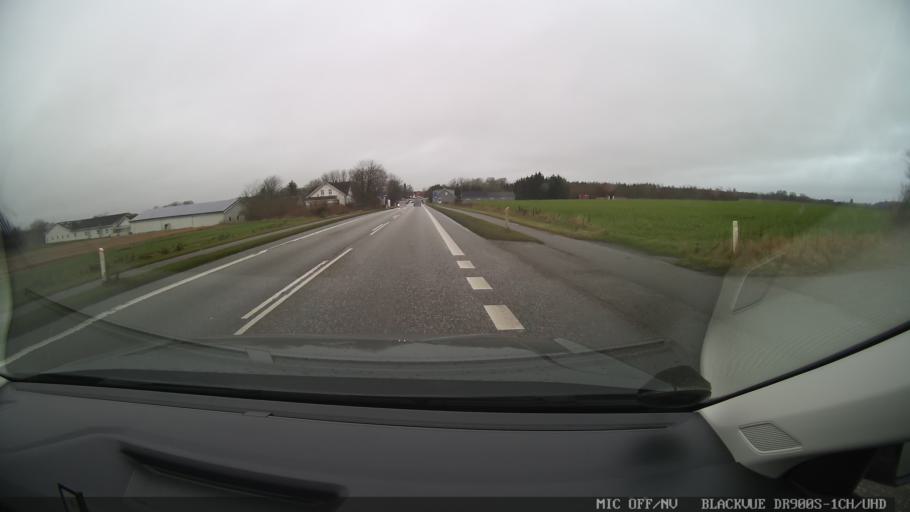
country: DK
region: Central Jutland
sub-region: Viborg Kommune
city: Karup
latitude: 56.3281
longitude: 9.2632
